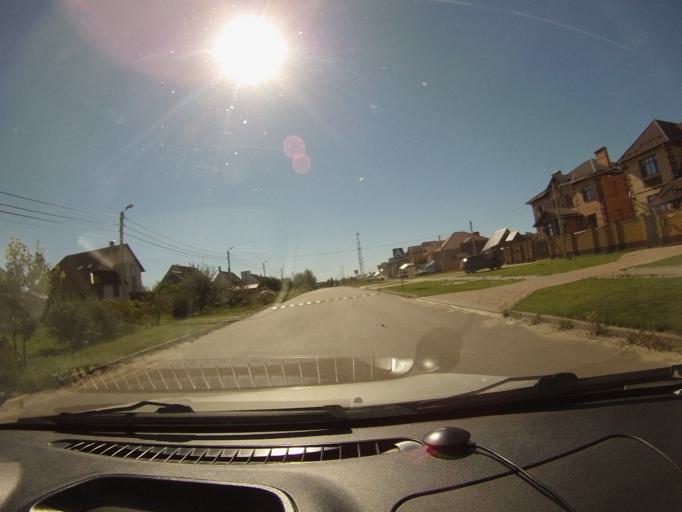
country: RU
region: Tambov
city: Tambov
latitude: 52.7678
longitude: 41.3808
